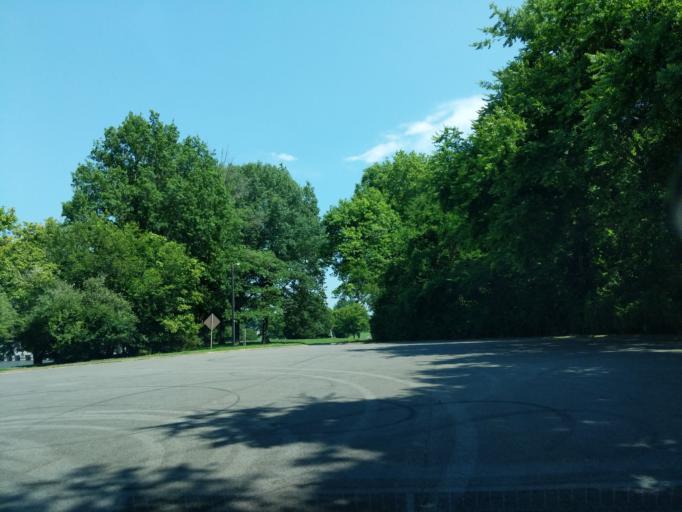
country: US
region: Tennessee
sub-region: Sumner County
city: Hendersonville
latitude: 36.2981
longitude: -86.6627
